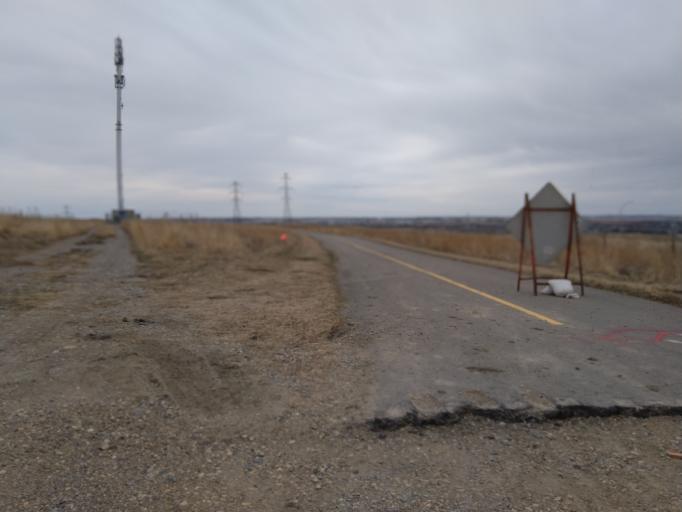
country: CA
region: Alberta
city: Calgary
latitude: 51.1761
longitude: -114.0678
